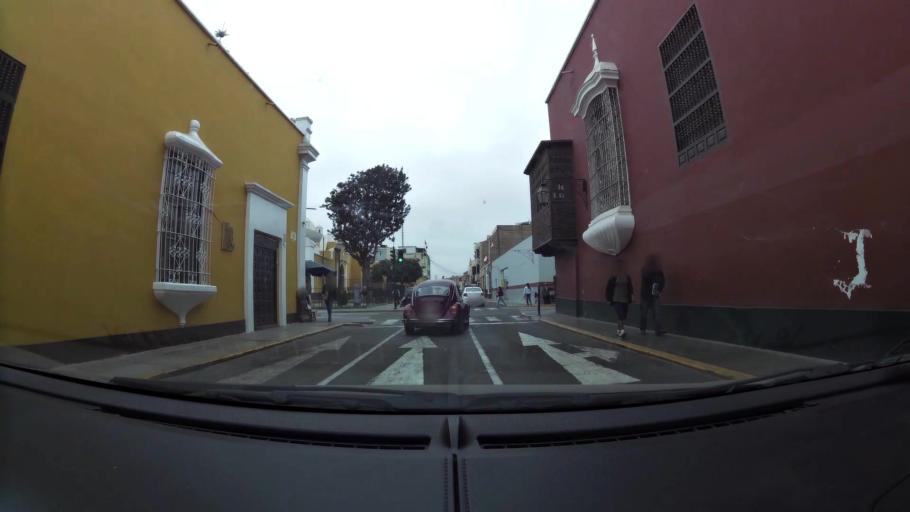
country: PE
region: La Libertad
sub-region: Provincia de Trujillo
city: Trujillo
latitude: -8.1138
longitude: -79.0293
